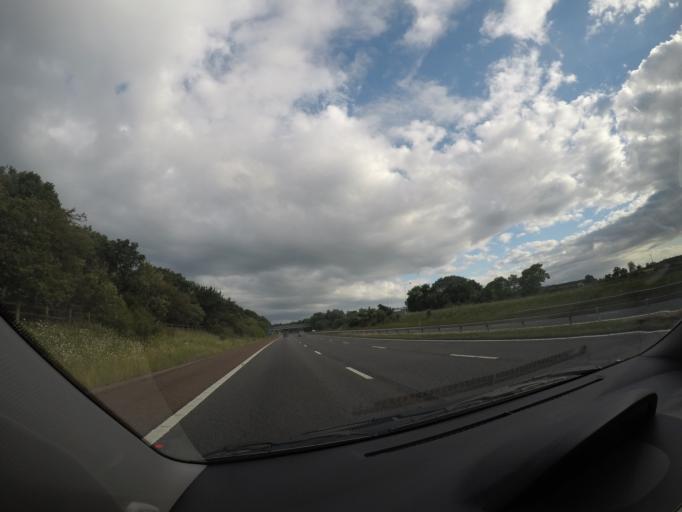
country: GB
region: England
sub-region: Cumbria
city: Scotby
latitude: 54.8011
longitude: -2.8710
